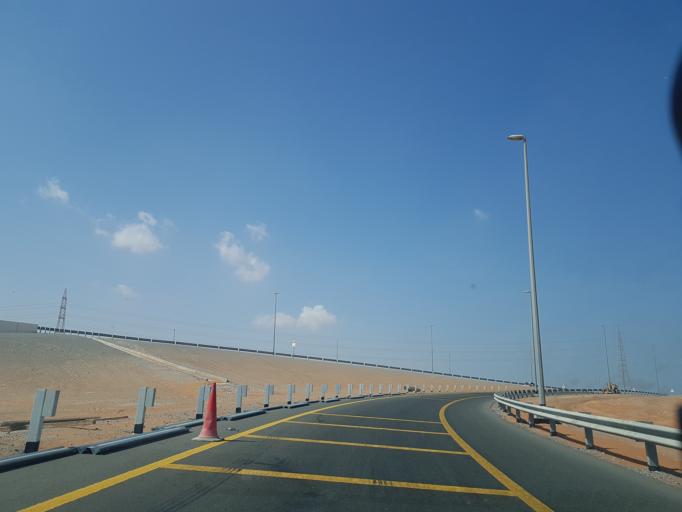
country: AE
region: Ra's al Khaymah
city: Ras al-Khaimah
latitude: 25.6961
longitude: 55.9261
